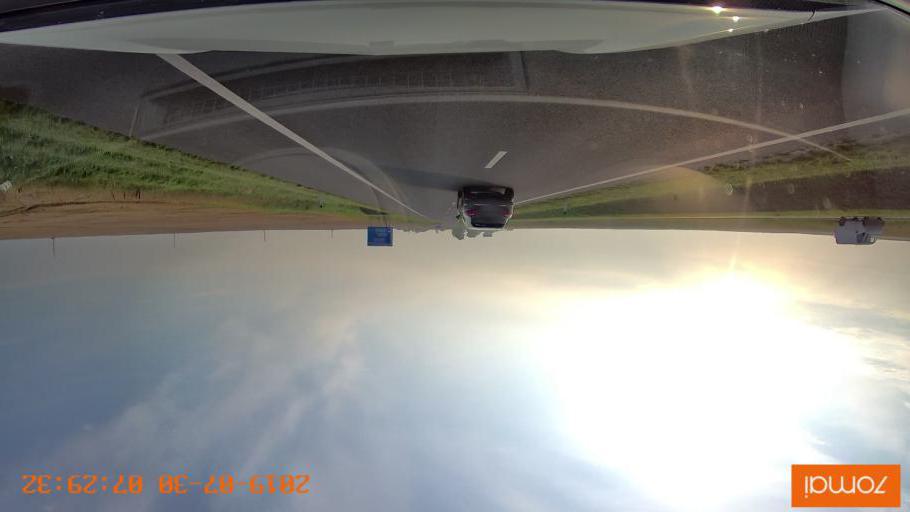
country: RU
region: Kaliningrad
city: Gvardeysk
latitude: 54.6718
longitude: 20.9418
